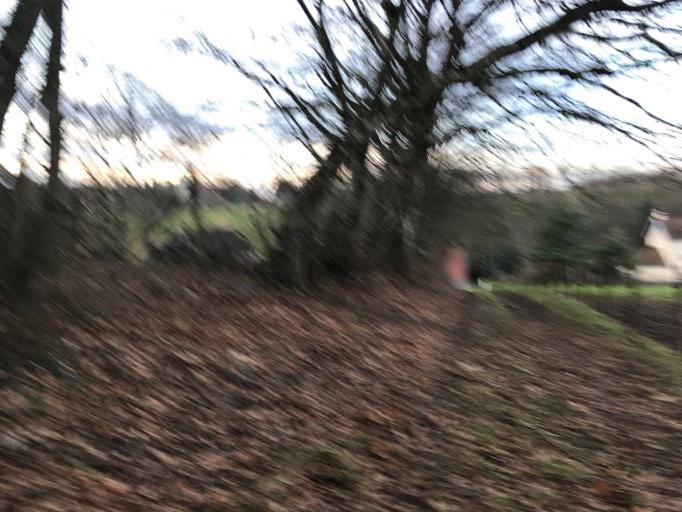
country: FR
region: Franche-Comte
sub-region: Departement du Jura
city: Orchamps
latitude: 47.1279
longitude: 5.6611
